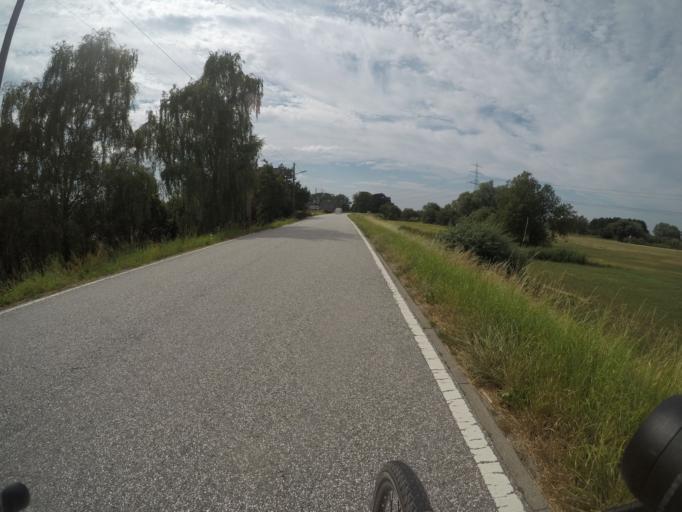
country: DE
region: Schleswig-Holstein
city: Oststeinbek
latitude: 53.4690
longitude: 10.1437
